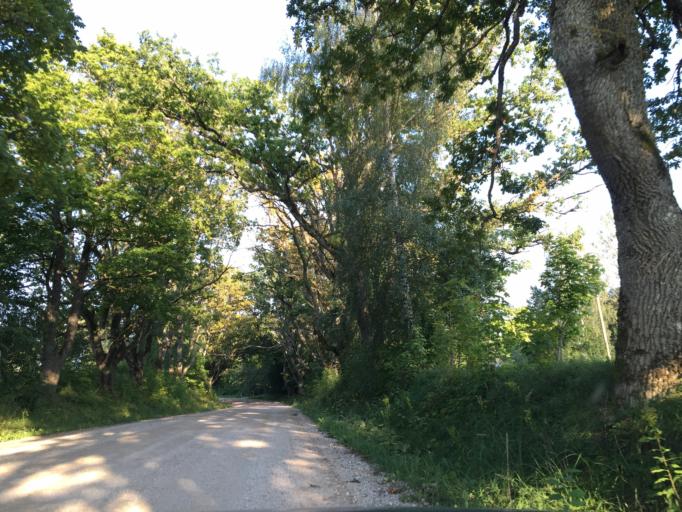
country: LV
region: Limbazu Rajons
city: Limbazi
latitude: 57.5505
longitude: 24.7873
